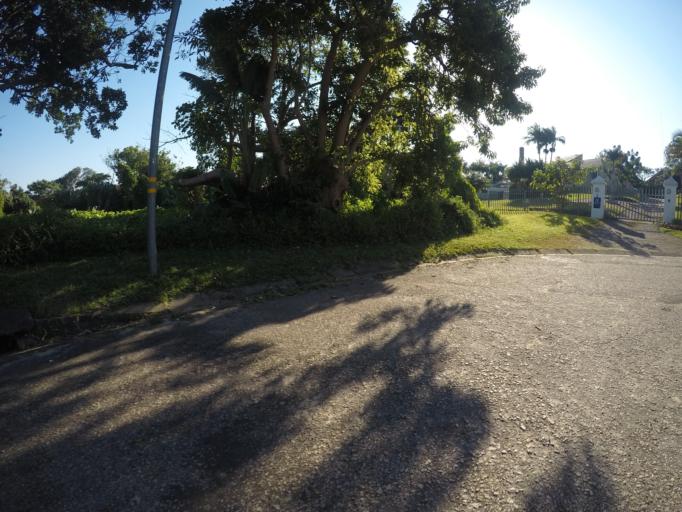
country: ZA
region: KwaZulu-Natal
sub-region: uThungulu District Municipality
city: Richards Bay
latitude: -28.7953
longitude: 32.0976
